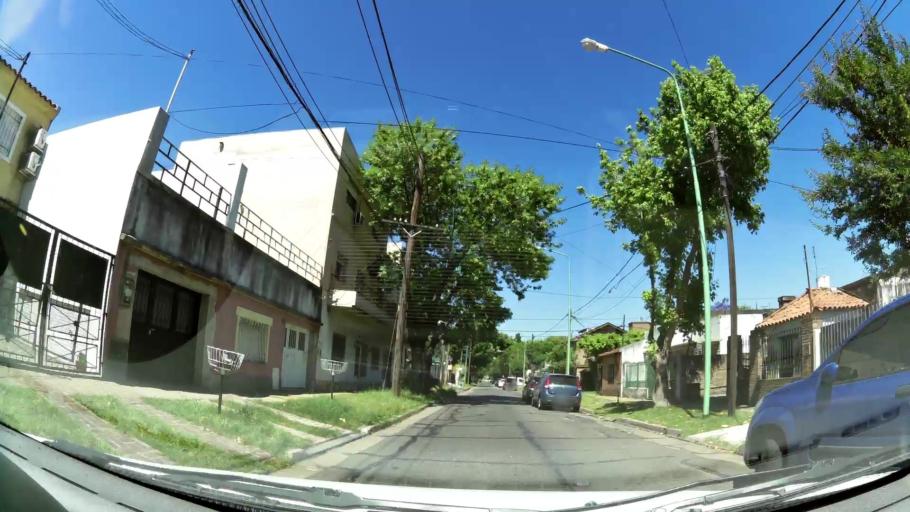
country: AR
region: Buenos Aires
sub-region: Partido de General San Martin
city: General San Martin
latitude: -34.5294
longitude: -58.5489
